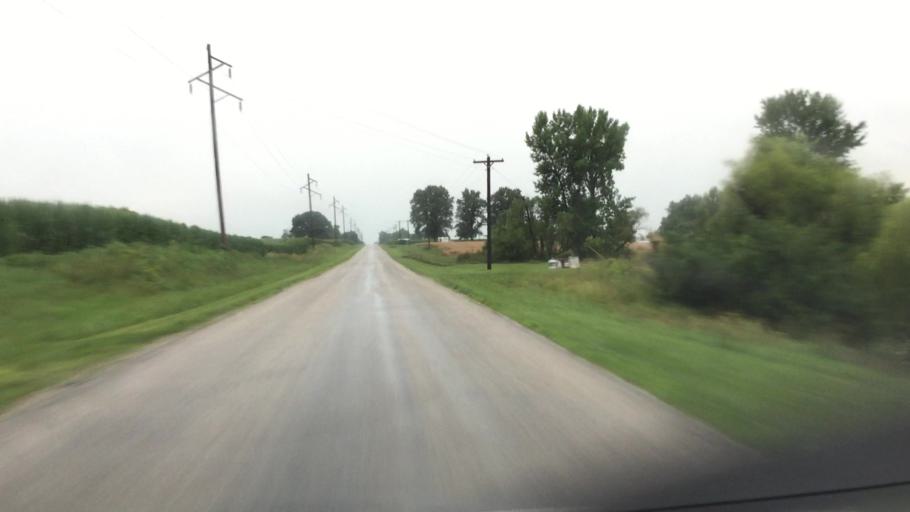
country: US
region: Illinois
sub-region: Hancock County
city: Hamilton
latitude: 40.4360
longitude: -91.2713
